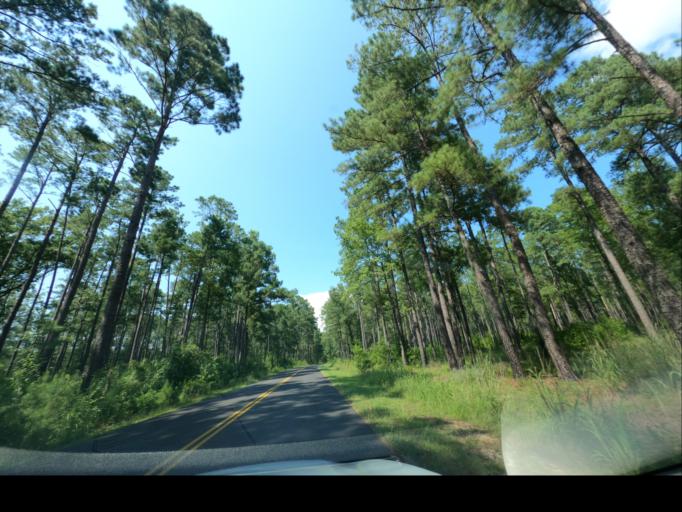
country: US
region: South Carolina
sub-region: Richland County
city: Gadsden
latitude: 33.8406
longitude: -80.8288
